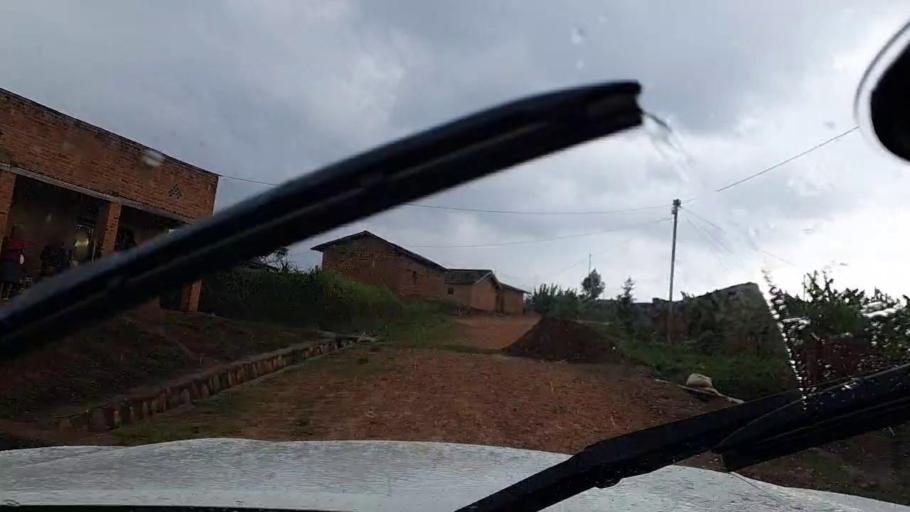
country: RW
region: Western Province
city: Kibuye
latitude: -2.1109
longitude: 29.4824
